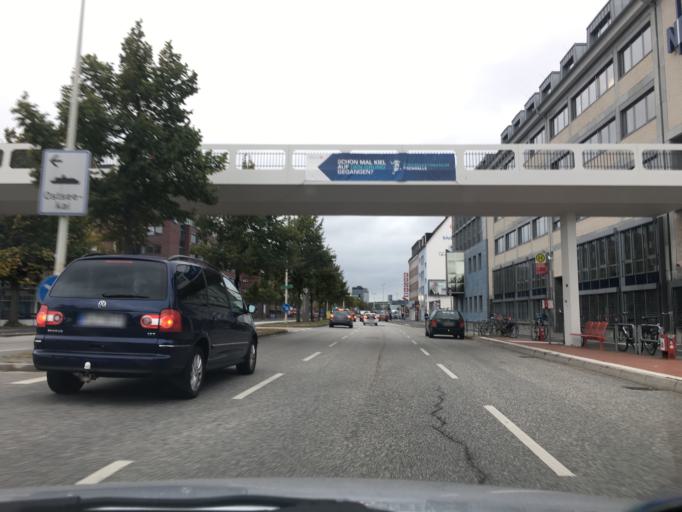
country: DE
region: Schleswig-Holstein
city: Kiel
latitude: 54.3235
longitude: 10.1435
